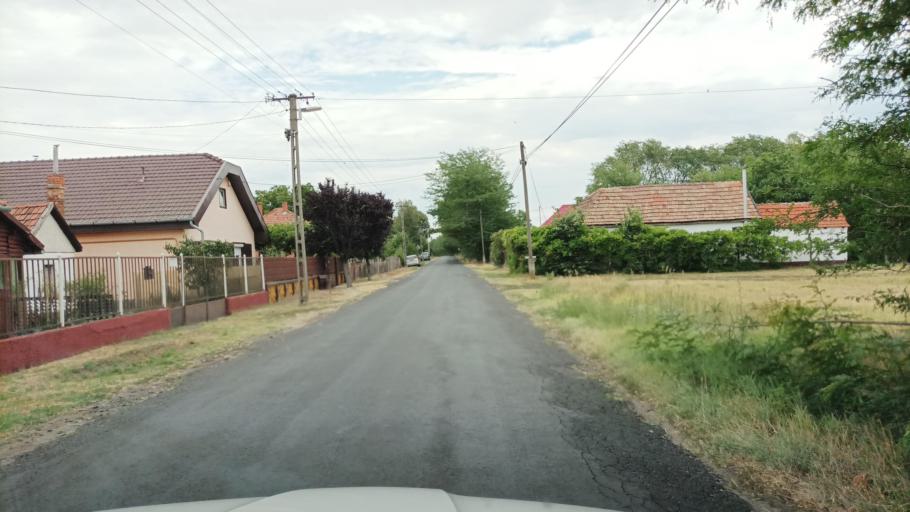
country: HU
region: Pest
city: Taborfalva
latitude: 47.1283
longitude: 19.4735
